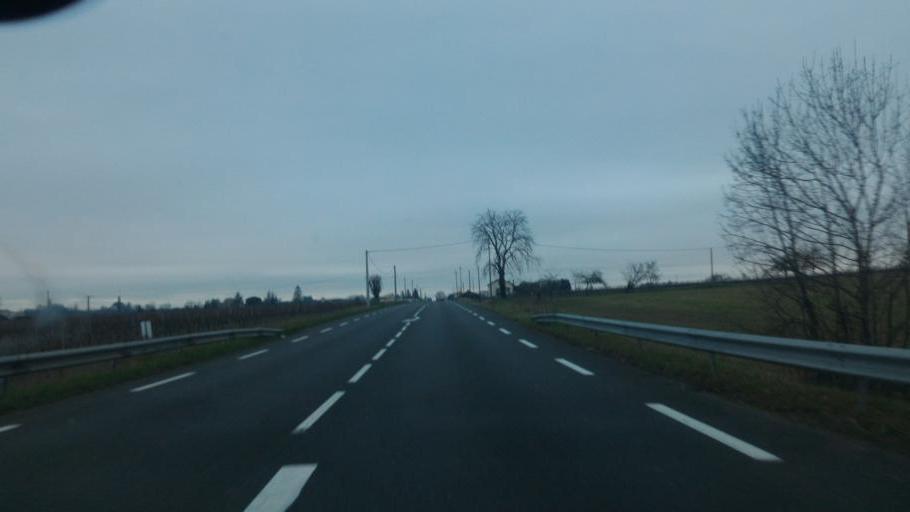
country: FR
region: Aquitaine
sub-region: Departement de la Gironde
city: Cars
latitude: 45.1251
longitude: -0.6002
